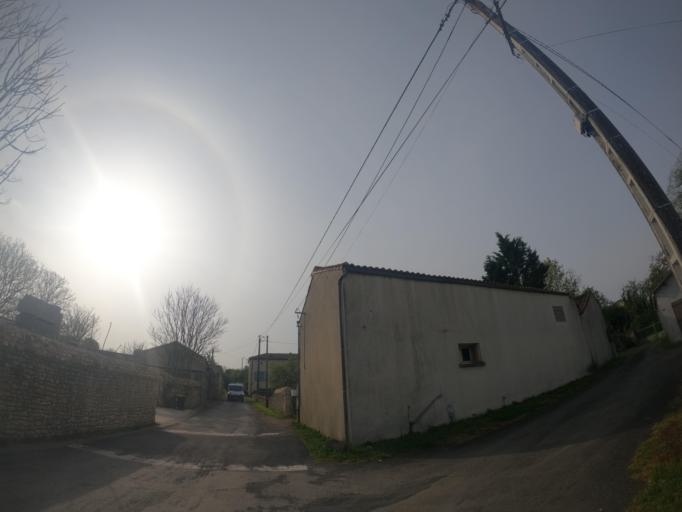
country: FR
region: Poitou-Charentes
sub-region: Departement des Deux-Sevres
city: Saint-Jean-de-Thouars
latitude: 46.9196
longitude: -0.1805
